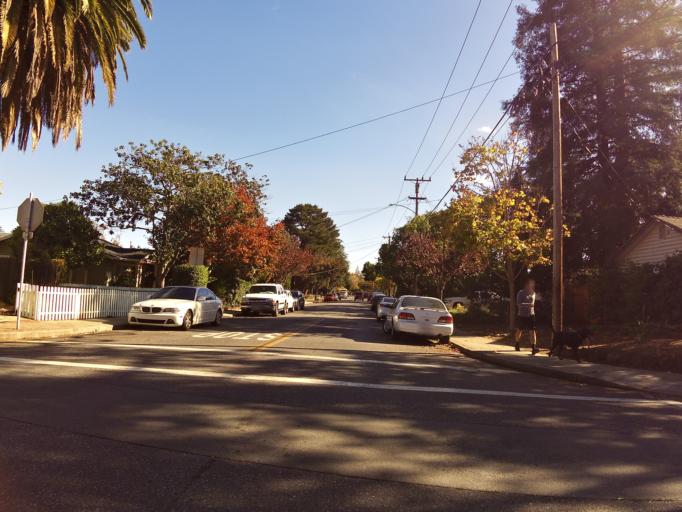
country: US
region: California
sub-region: Santa Clara County
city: Mountain View
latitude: 37.3923
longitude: -122.0911
